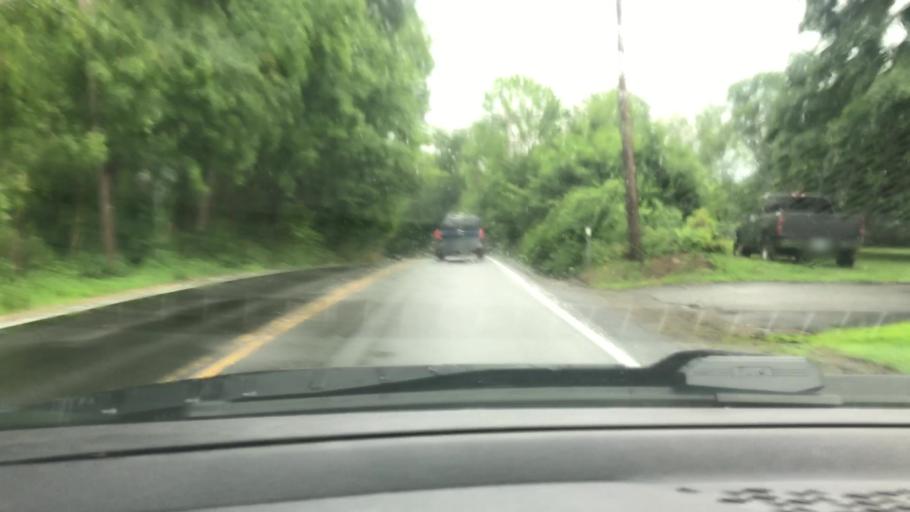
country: US
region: New Hampshire
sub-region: Merrimack County
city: Epsom
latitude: 43.1703
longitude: -71.2550
